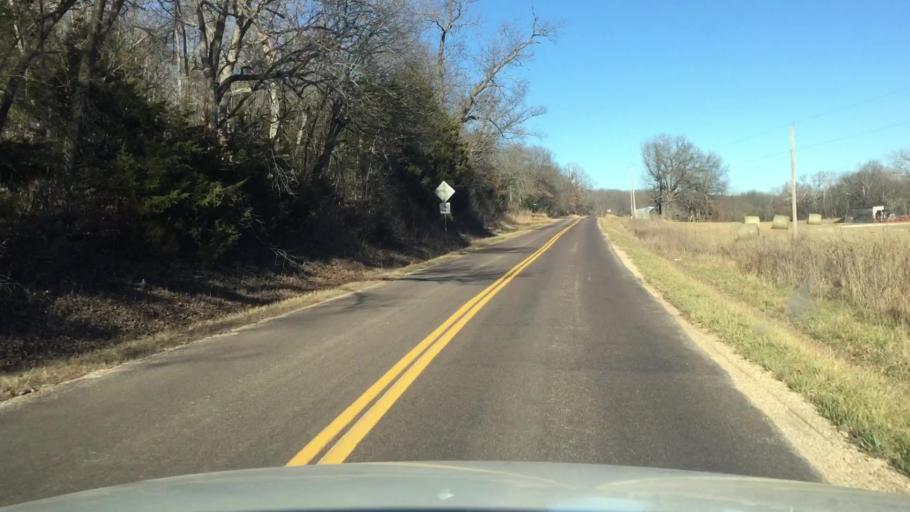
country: US
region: Missouri
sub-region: Miller County
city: Eldon
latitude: 38.3431
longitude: -92.7078
